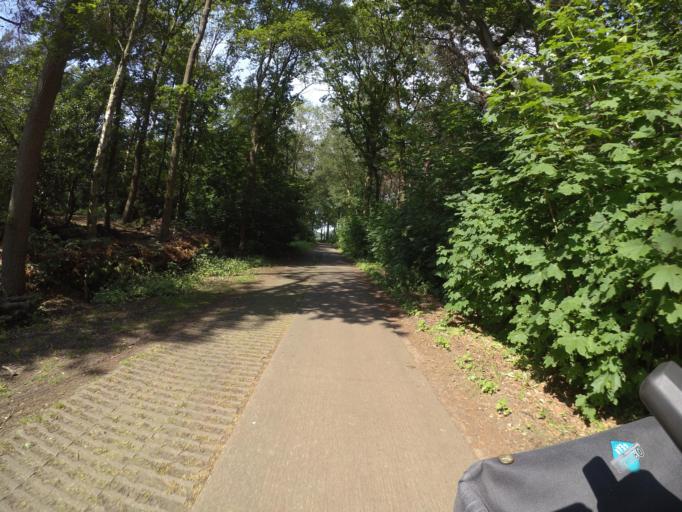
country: NL
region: Overijssel
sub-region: Gemeente Raalte
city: Raalte
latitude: 52.4390
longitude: 6.3058
